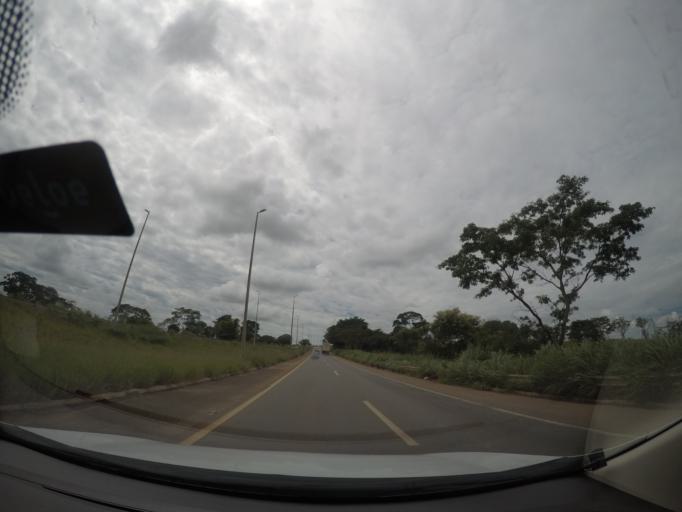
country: BR
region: Goias
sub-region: Inhumas
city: Inhumas
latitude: -16.4034
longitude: -49.4845
